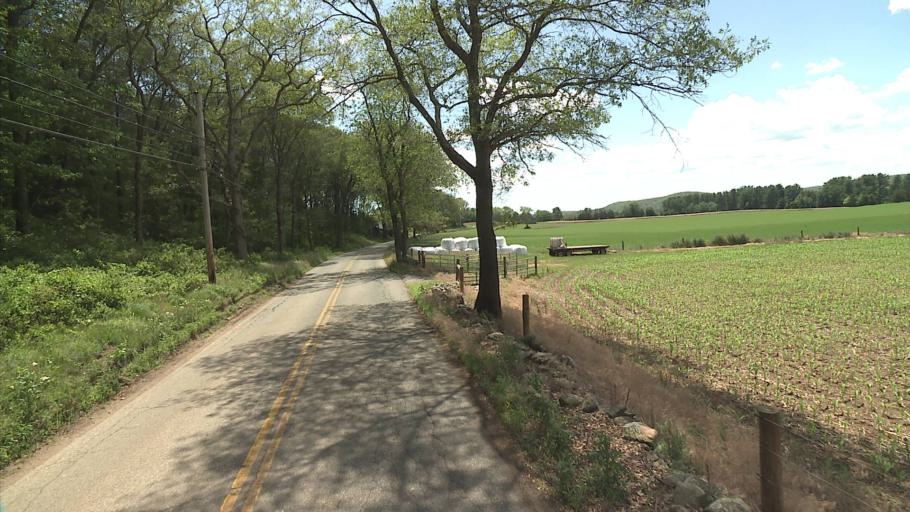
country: US
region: Connecticut
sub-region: New London County
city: Preston City
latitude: 41.5488
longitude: -71.8832
